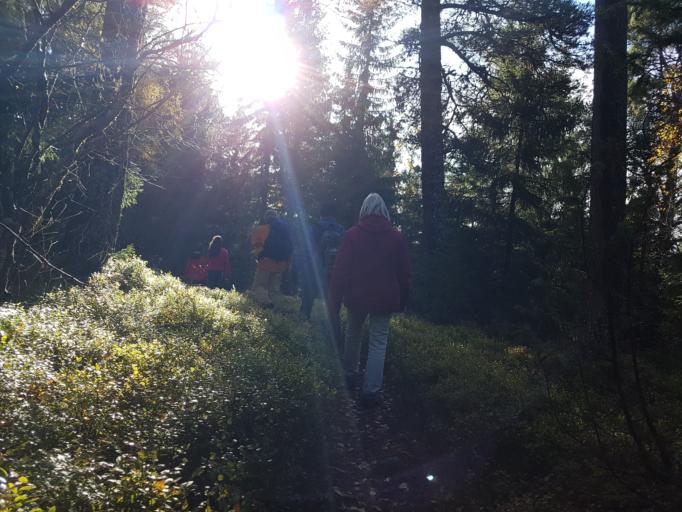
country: NO
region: Sor-Trondelag
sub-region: Trondheim
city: Trondheim
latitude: 63.4238
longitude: 10.2938
